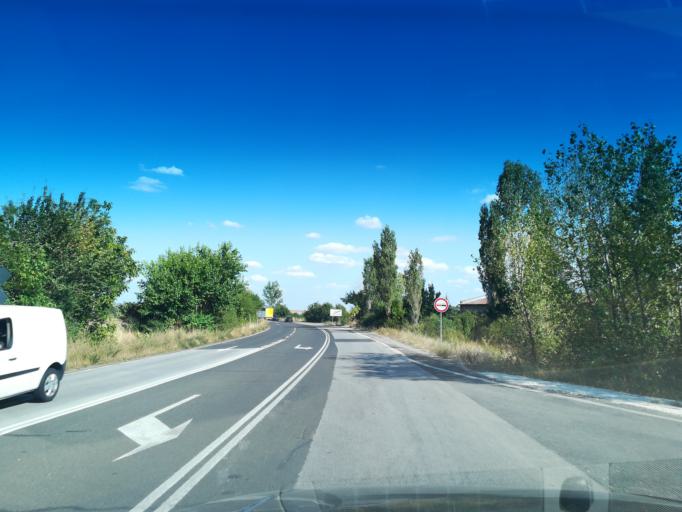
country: BG
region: Stara Zagora
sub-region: Obshtina Chirpan
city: Chirpan
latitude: 42.0722
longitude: 25.1997
